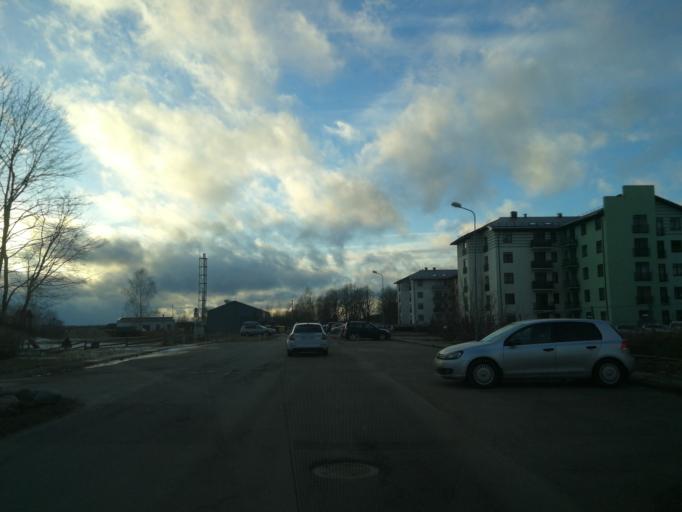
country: LV
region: Adazi
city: Adazi
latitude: 57.0701
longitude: 24.3565
